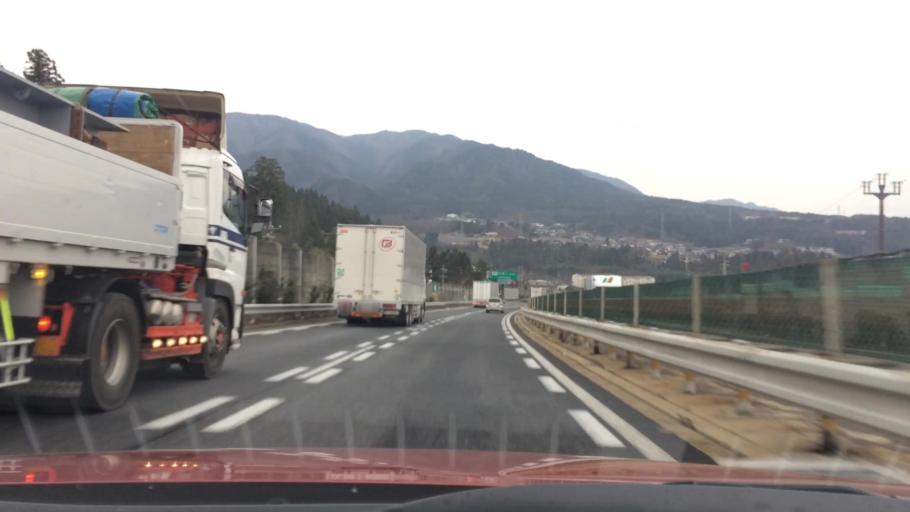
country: JP
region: Gifu
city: Nakatsugawa
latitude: 35.4825
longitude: 137.5099
